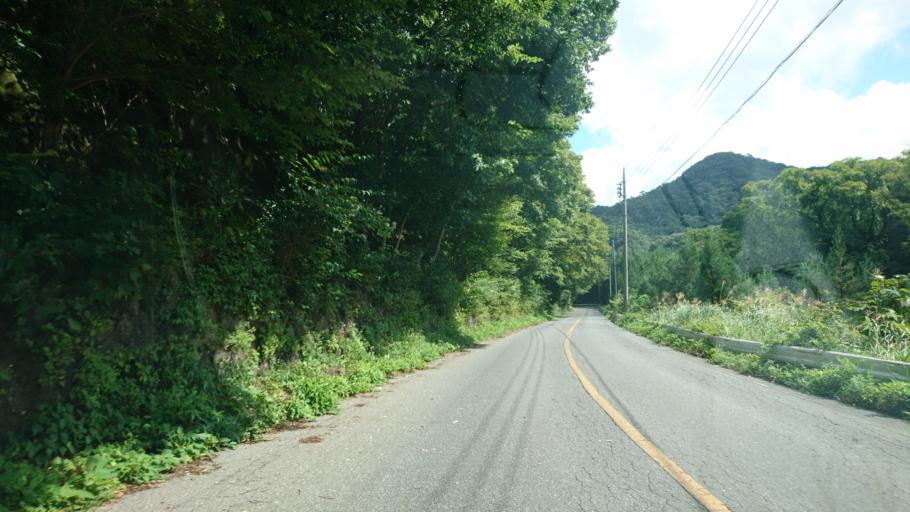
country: JP
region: Gunma
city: Omamacho-omama
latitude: 36.5925
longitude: 139.2334
